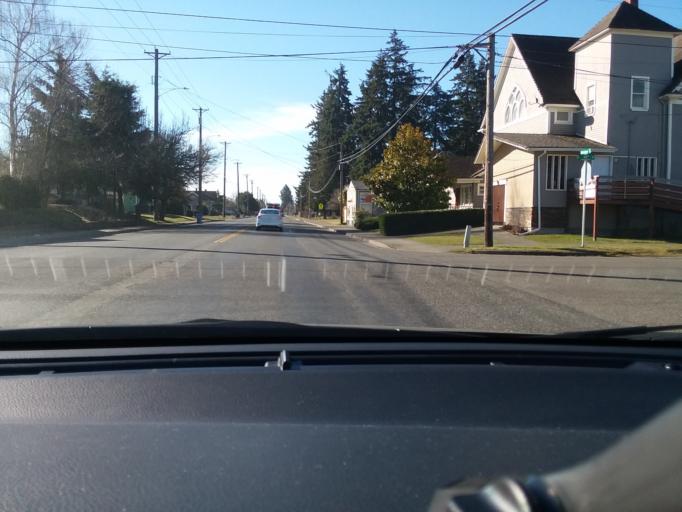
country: US
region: Washington
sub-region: Pierce County
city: Tacoma
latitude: 47.2128
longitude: -122.4209
